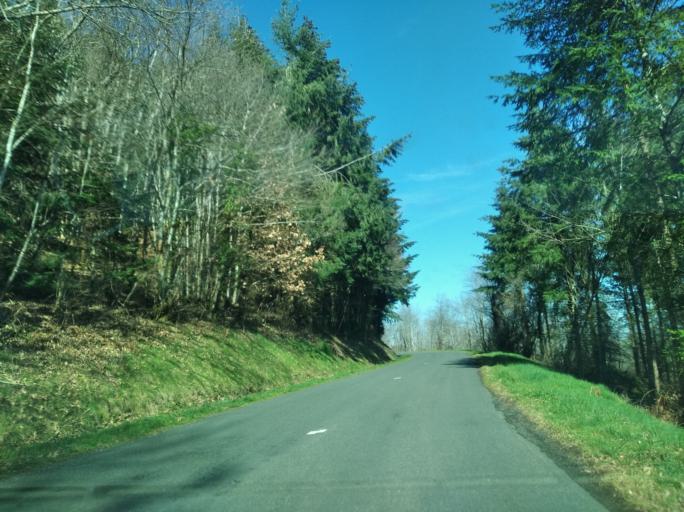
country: FR
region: Auvergne
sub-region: Departement de l'Allier
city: Le Mayet-de-Montagne
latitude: 46.1034
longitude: 3.6912
